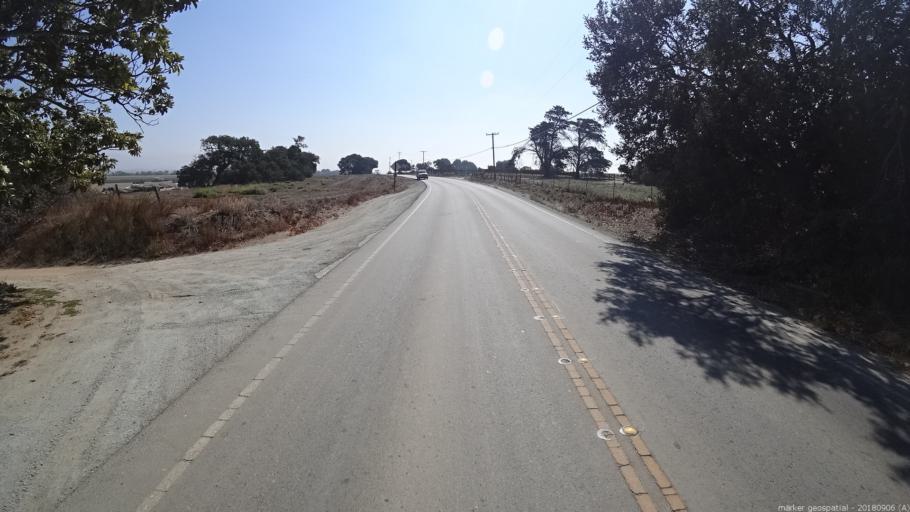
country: US
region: California
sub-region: Monterey County
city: Chualar
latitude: 36.5628
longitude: -121.5621
